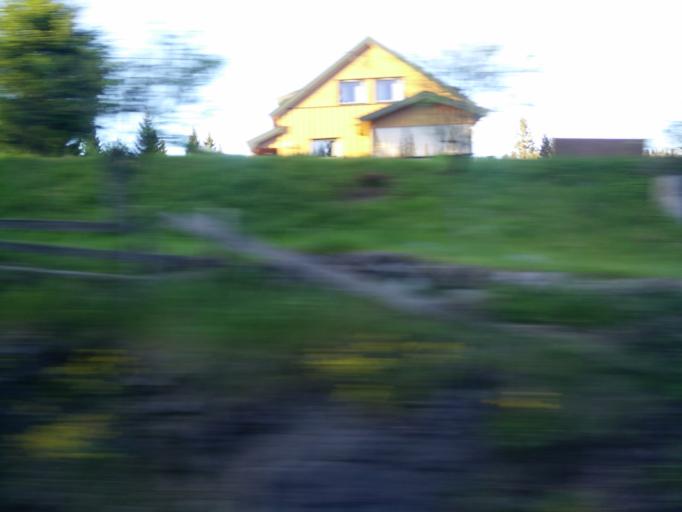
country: NO
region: Akershus
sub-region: Baerum
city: Skui
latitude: 59.9550
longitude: 10.3740
